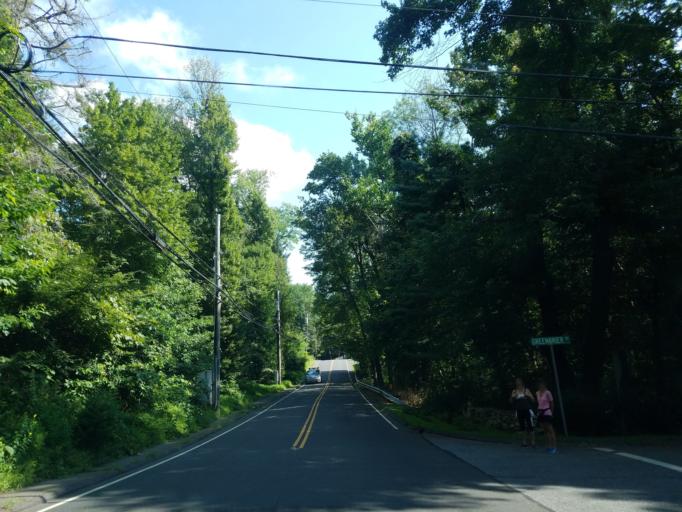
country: US
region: Connecticut
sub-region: Fairfield County
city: Westport
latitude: 41.1813
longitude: -73.3448
